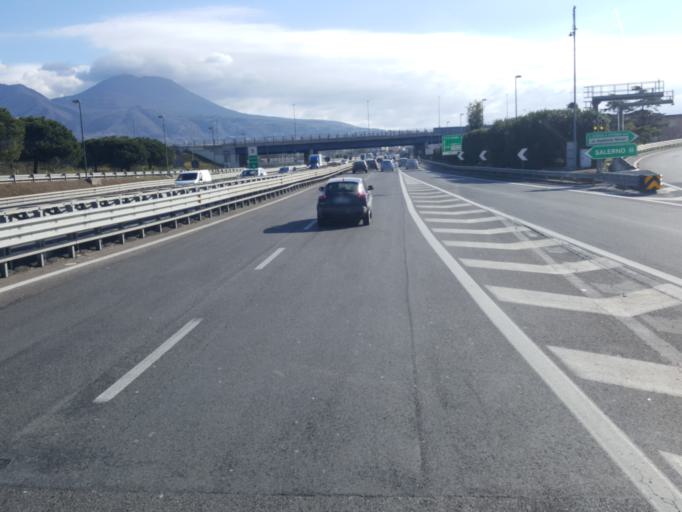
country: IT
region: Campania
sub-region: Provincia di Napoli
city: San Giorgio a Cremano
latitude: 40.8411
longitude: 14.3293
